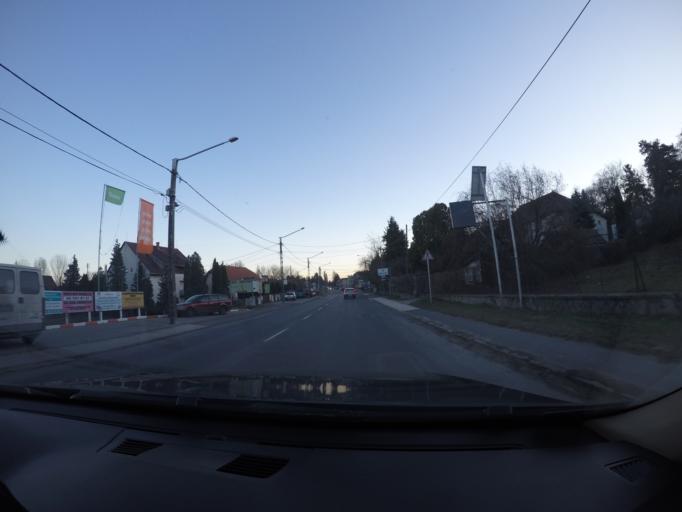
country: HU
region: Pest
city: Tahitotfalu
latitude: 47.7532
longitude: 19.0767
